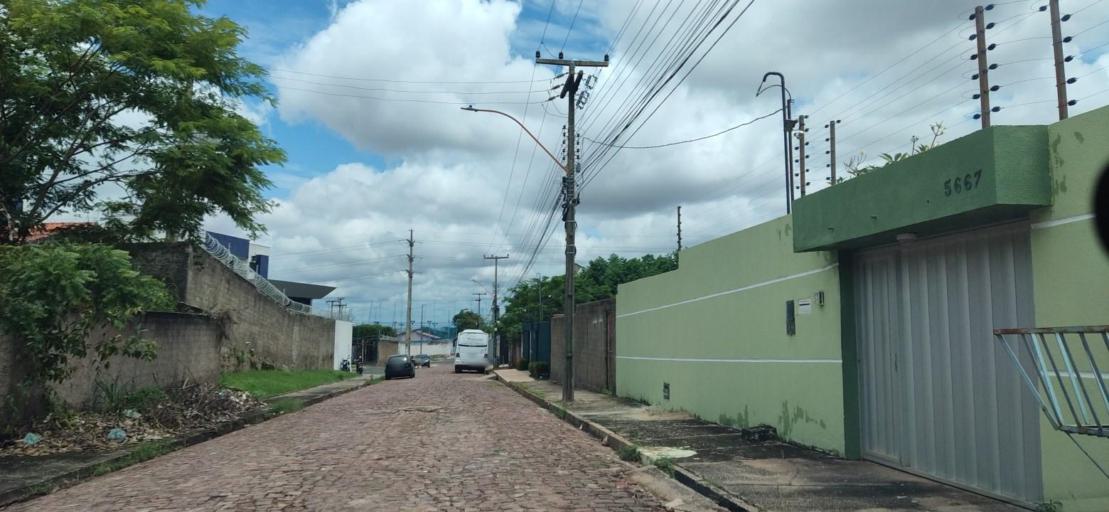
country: BR
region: Piaui
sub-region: Teresina
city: Teresina
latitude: -5.0723
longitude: -42.7504
